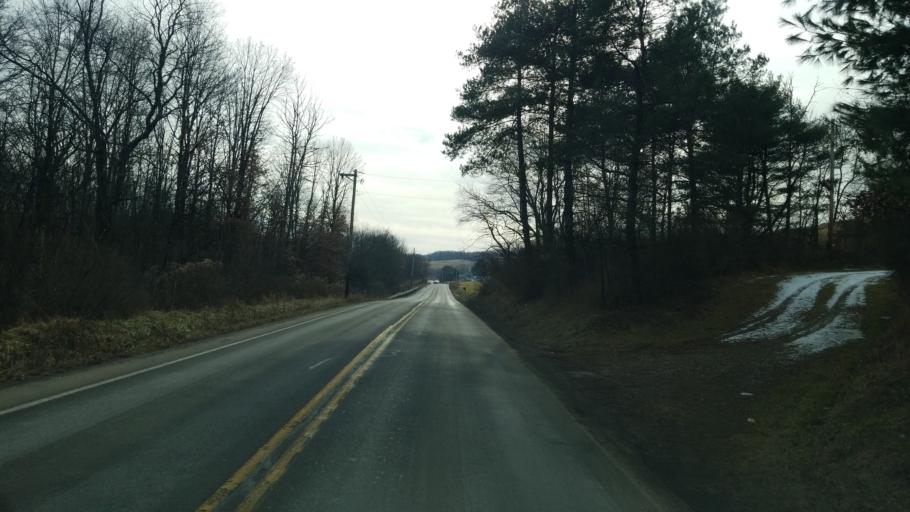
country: US
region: Pennsylvania
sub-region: Jefferson County
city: Punxsutawney
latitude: 40.9015
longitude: -79.0402
